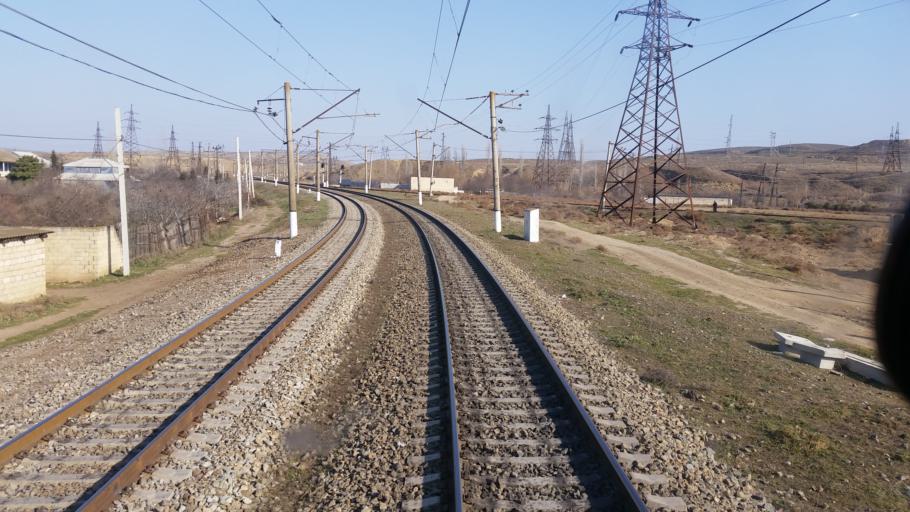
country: AZ
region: Haciqabul
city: Haciqabul
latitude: 40.0417
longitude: 48.9497
